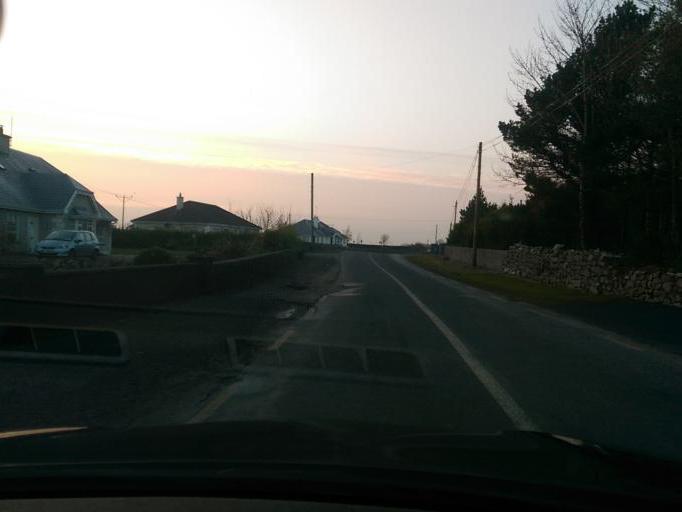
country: IE
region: Connaught
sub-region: County Galway
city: Athenry
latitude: 53.2636
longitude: -8.6858
